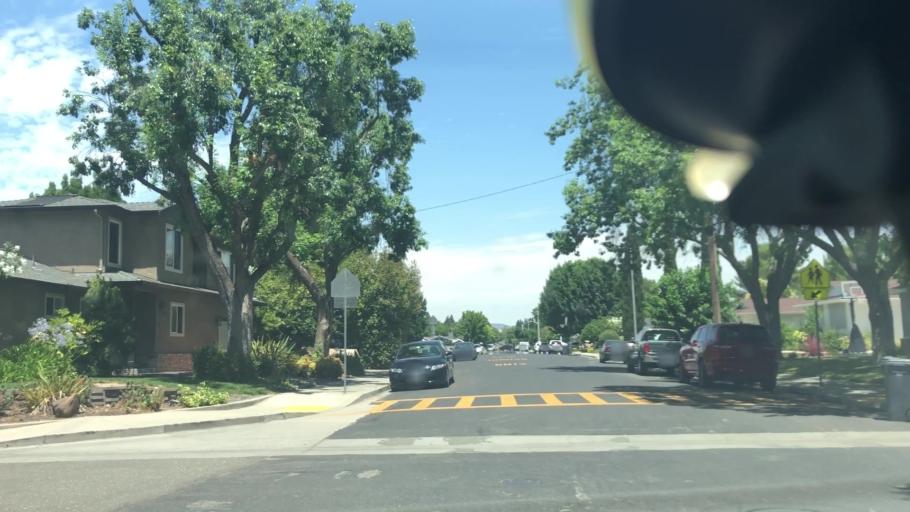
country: US
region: California
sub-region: Alameda County
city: Pleasanton
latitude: 37.6712
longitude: -121.8689
